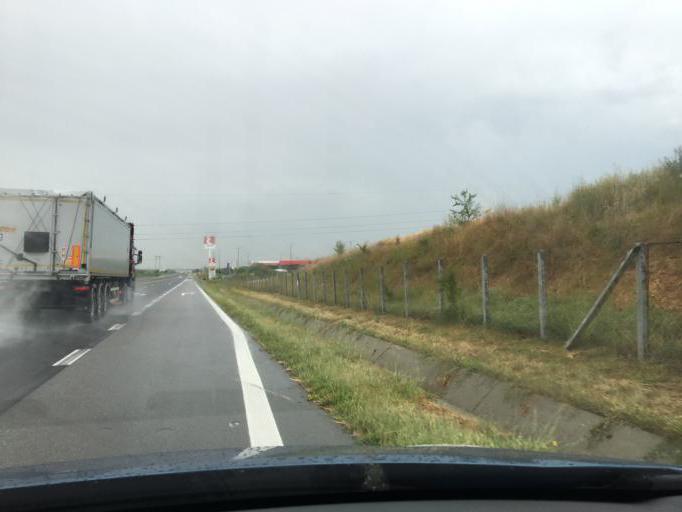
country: BG
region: Sliven
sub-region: Obshtina Nova Zagora
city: Nova Zagora
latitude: 42.4520
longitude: 26.0496
